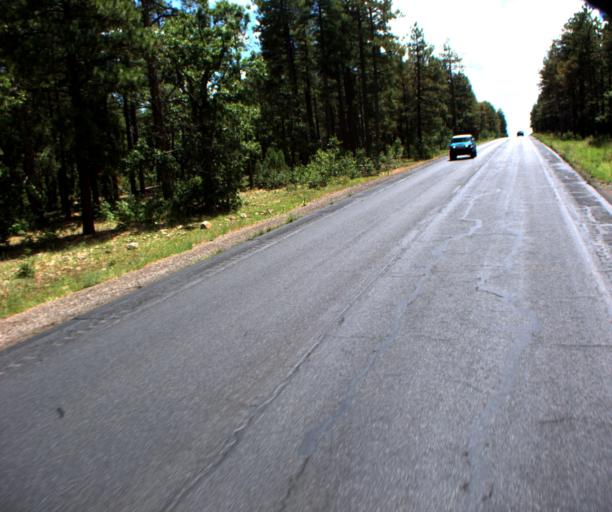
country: US
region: Arizona
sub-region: Gila County
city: Pine
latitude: 34.4915
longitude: -111.4576
